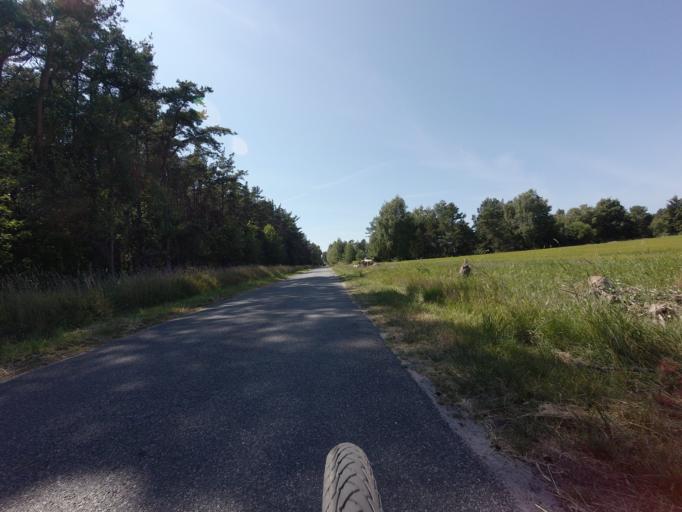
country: DK
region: North Denmark
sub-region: Laeso Kommune
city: Byrum
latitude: 57.2914
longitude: 10.9575
